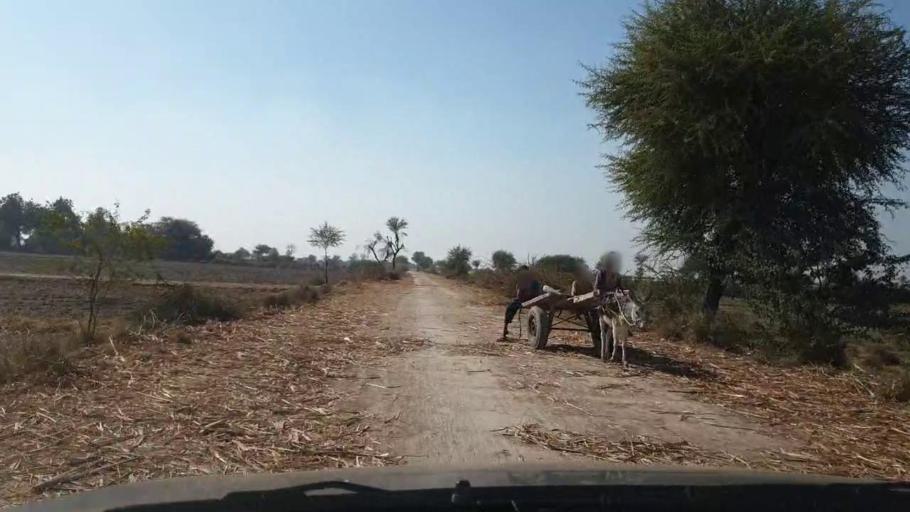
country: PK
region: Sindh
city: Jhol
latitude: 25.9289
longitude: 68.7983
